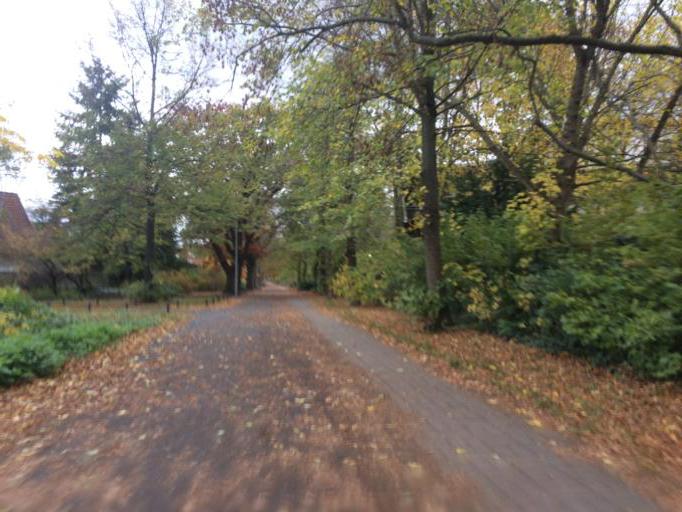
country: DE
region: Berlin
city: Tegel
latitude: 52.5897
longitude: 13.3041
